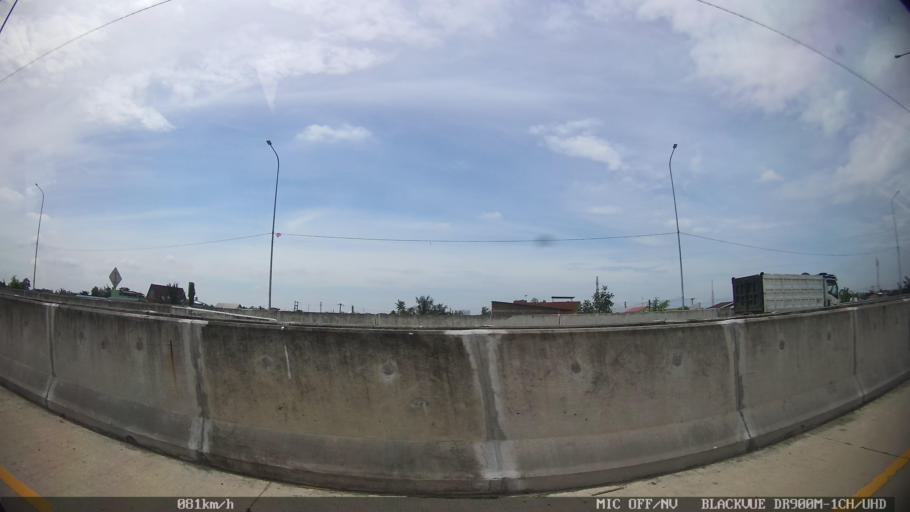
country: ID
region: North Sumatra
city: Medan
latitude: 3.6476
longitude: 98.6728
